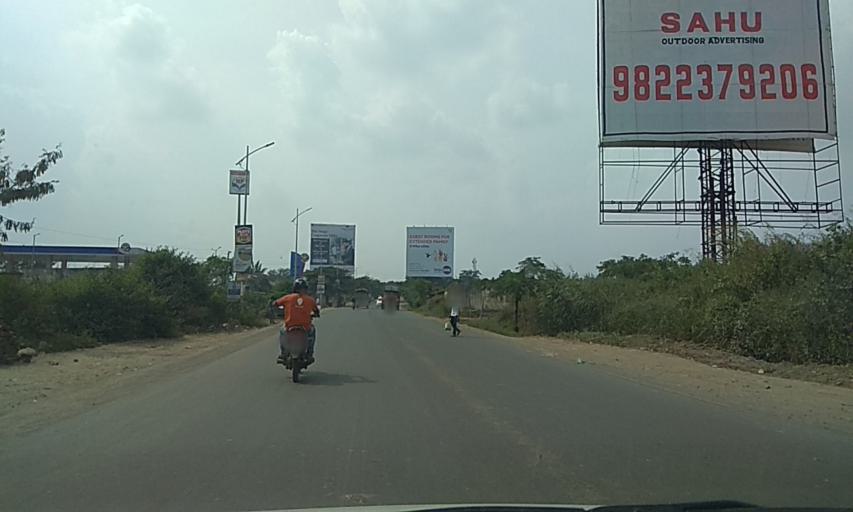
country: IN
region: Maharashtra
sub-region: Pune Division
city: Pimpri
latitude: 18.5810
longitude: 73.7227
